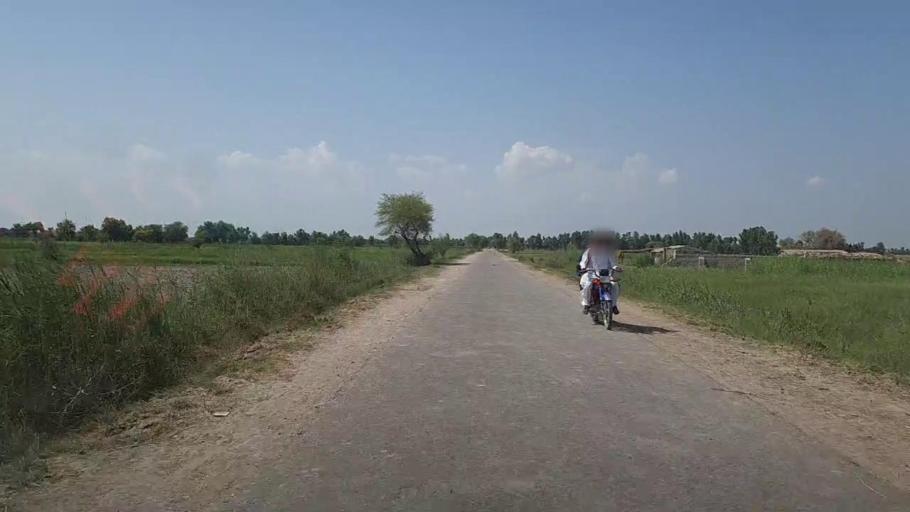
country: PK
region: Sindh
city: Khairpur
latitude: 28.0781
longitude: 69.6377
